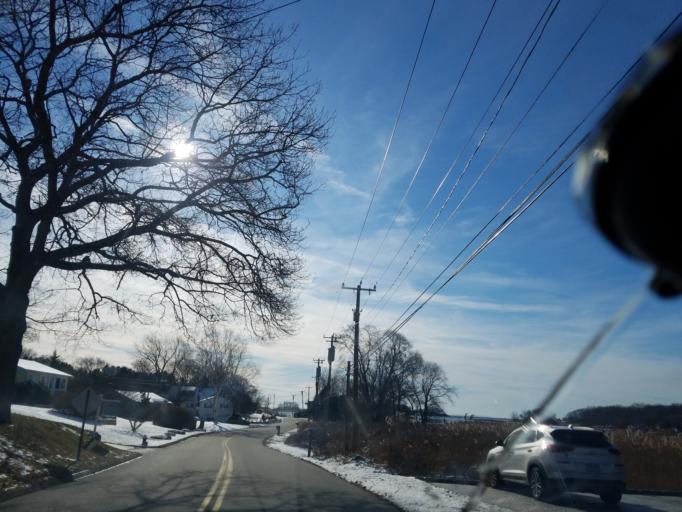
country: US
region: Connecticut
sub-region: New London County
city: Niantic
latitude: 41.3091
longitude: -72.2172
